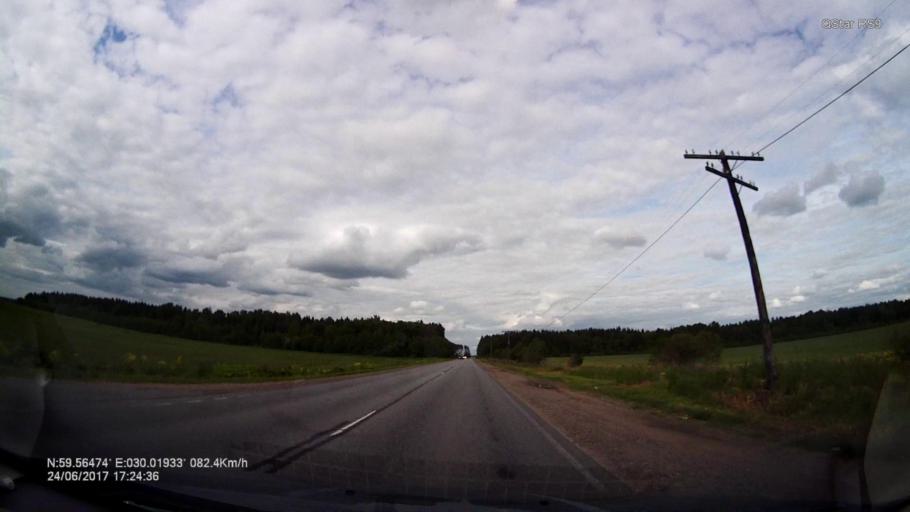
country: RU
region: Leningrad
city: Mariyenburg
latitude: 59.5648
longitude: 30.0196
